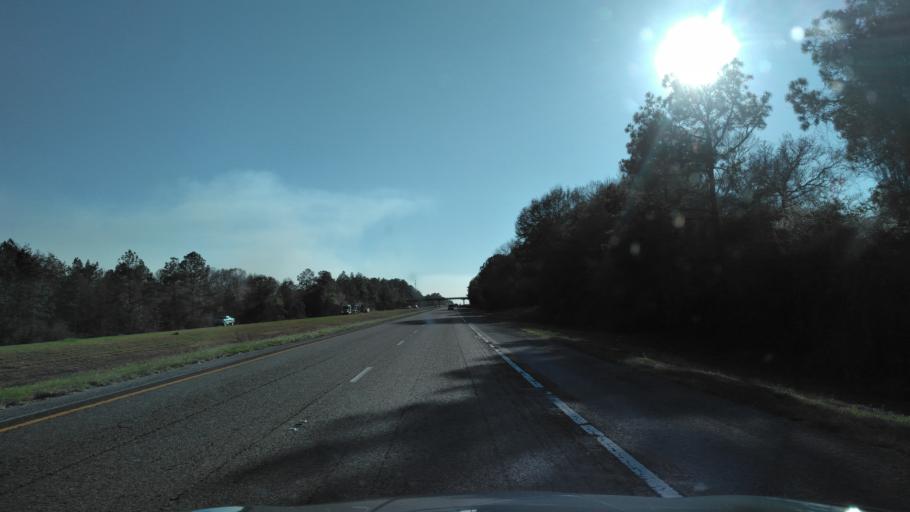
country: US
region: Alabama
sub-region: Baldwin County
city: Bay Minette
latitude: 31.0015
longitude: -87.6832
